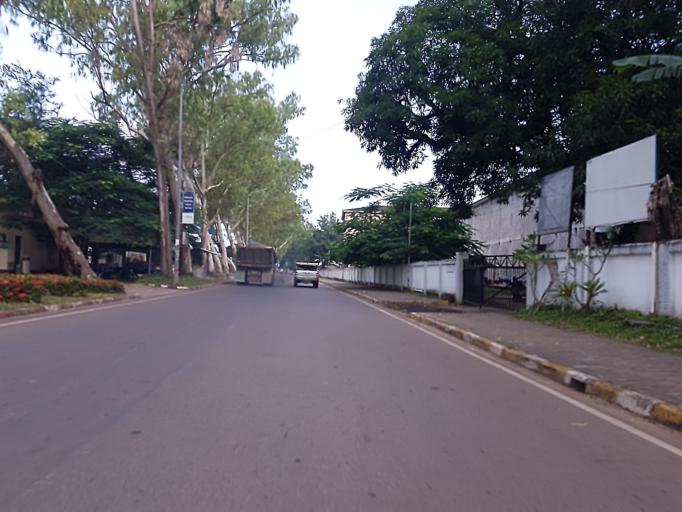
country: LA
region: Vientiane
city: Vientiane
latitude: 17.9591
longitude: 102.6125
